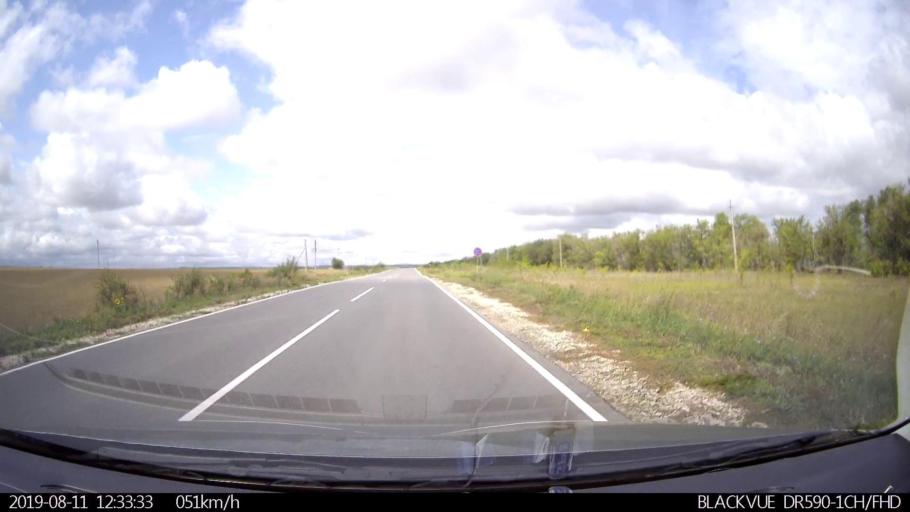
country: RU
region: Ulyanovsk
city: Ignatovka
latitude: 53.8102
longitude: 47.8545
